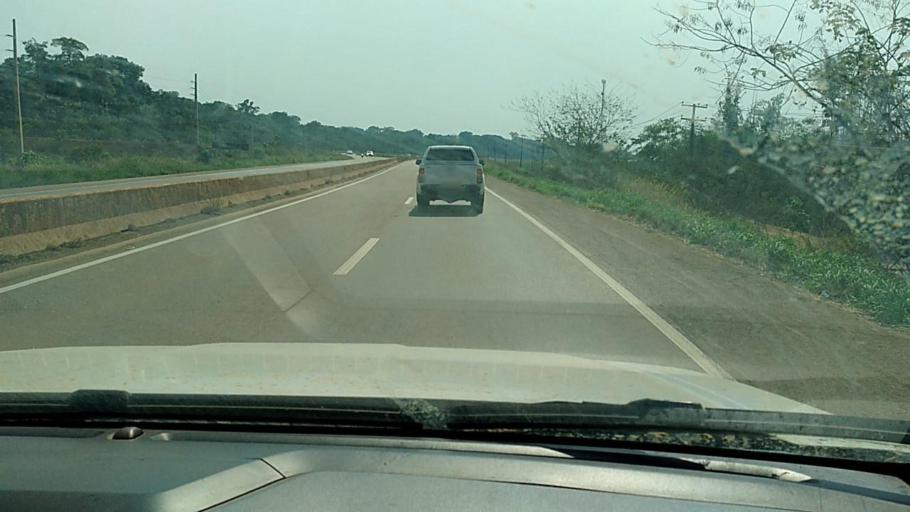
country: BR
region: Rondonia
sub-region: Porto Velho
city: Porto Velho
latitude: -8.8032
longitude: -63.7470
